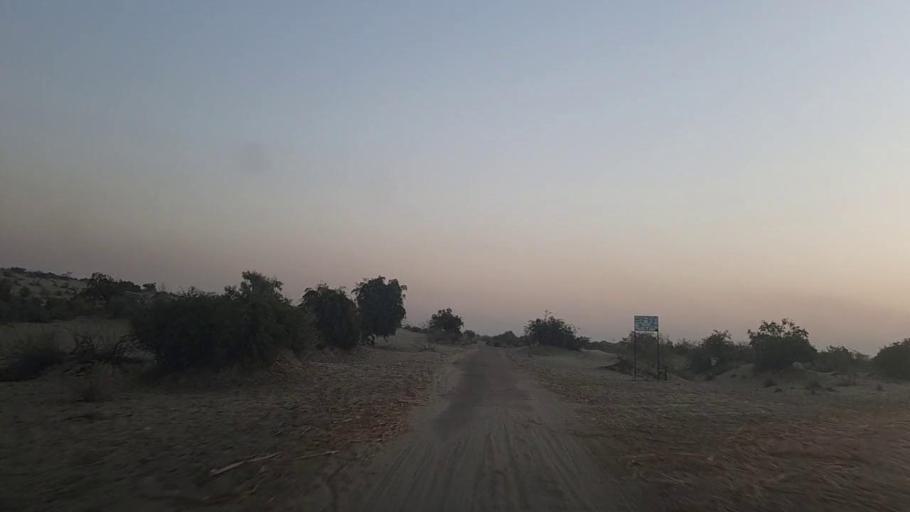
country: PK
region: Sindh
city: Jam Sahib
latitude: 26.3962
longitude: 68.8095
